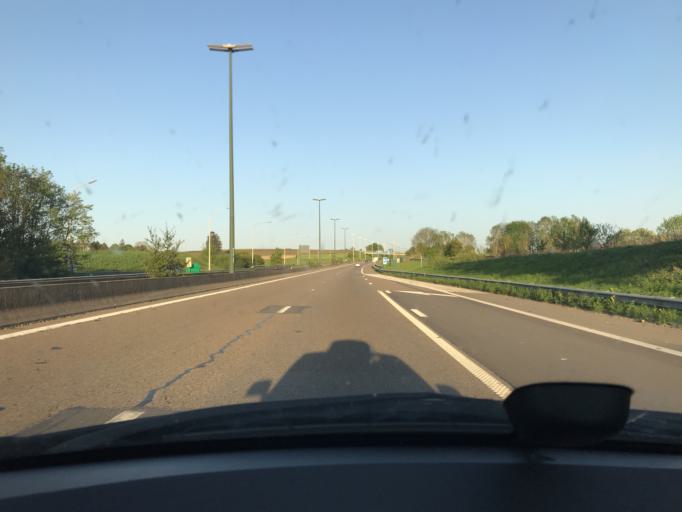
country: BE
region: Wallonia
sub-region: Province du Luxembourg
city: Neufchateau
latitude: 49.8744
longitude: 5.4833
